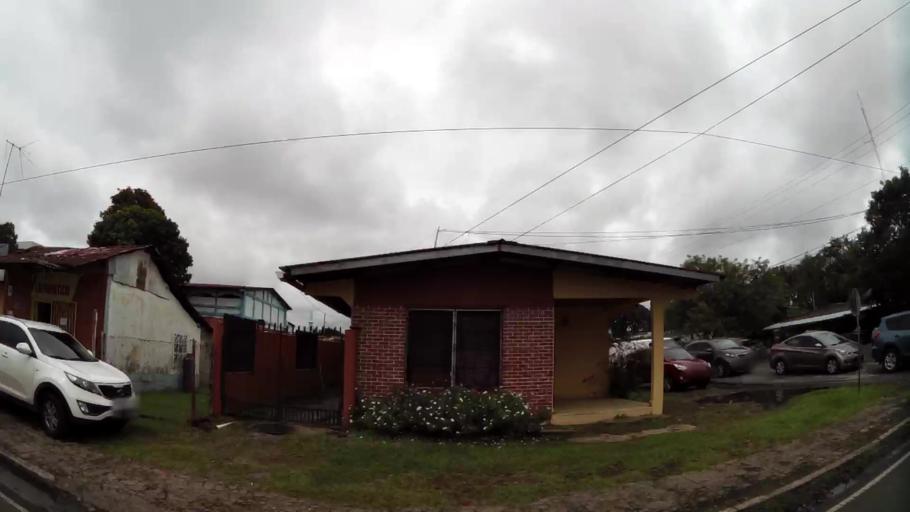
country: PA
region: Chiriqui
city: David
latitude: 8.4248
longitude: -82.4299
